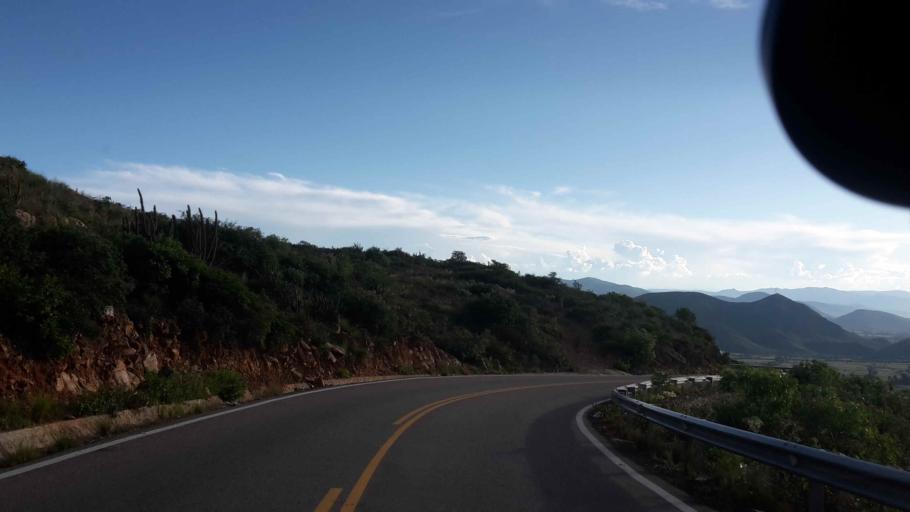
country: BO
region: Cochabamba
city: Arani
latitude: -17.5863
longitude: -65.7508
